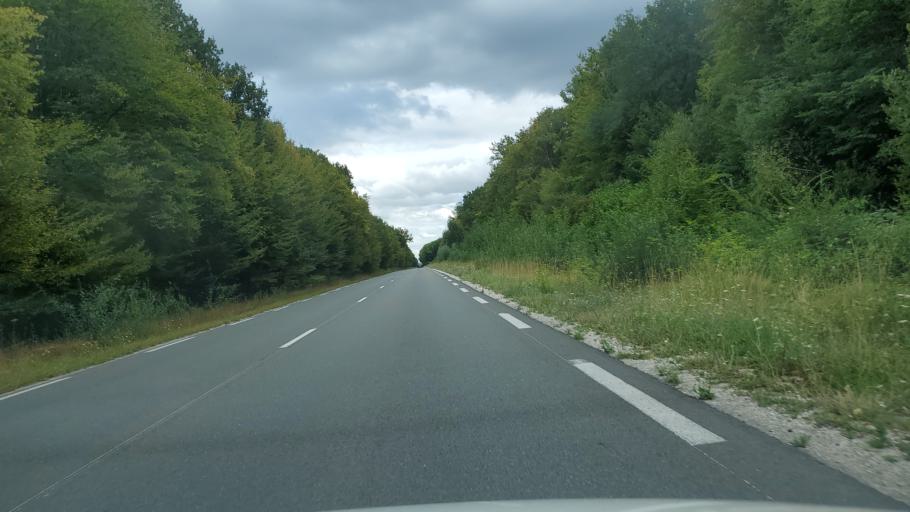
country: FR
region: Ile-de-France
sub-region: Departement de Seine-et-Marne
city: Mortcerf
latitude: 48.7709
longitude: 2.9088
